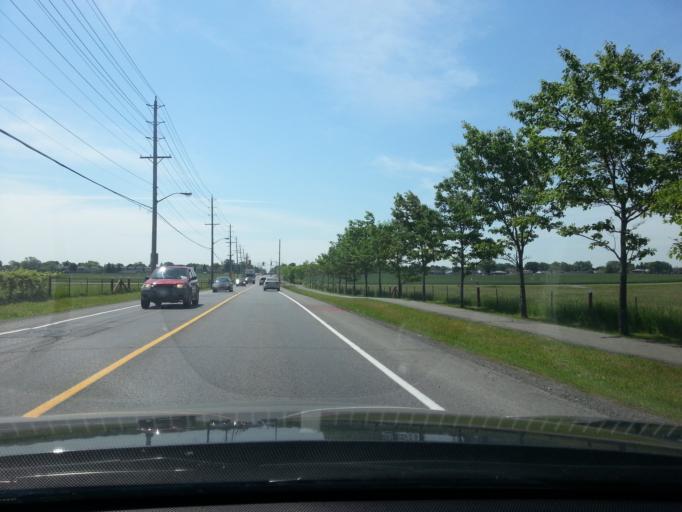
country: CA
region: Ontario
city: Ottawa
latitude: 45.3764
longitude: -75.7195
